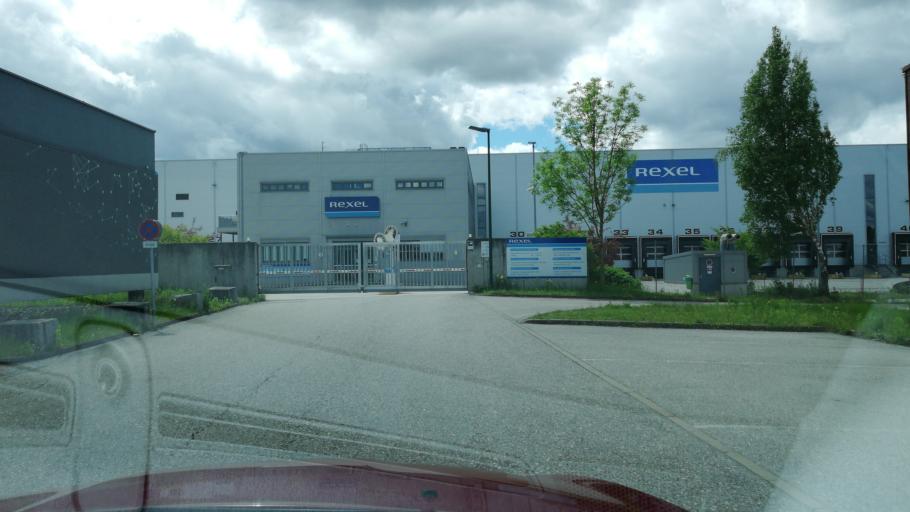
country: AT
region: Upper Austria
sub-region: Wels-Land
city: Marchtrenk
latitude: 48.1686
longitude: 14.1249
